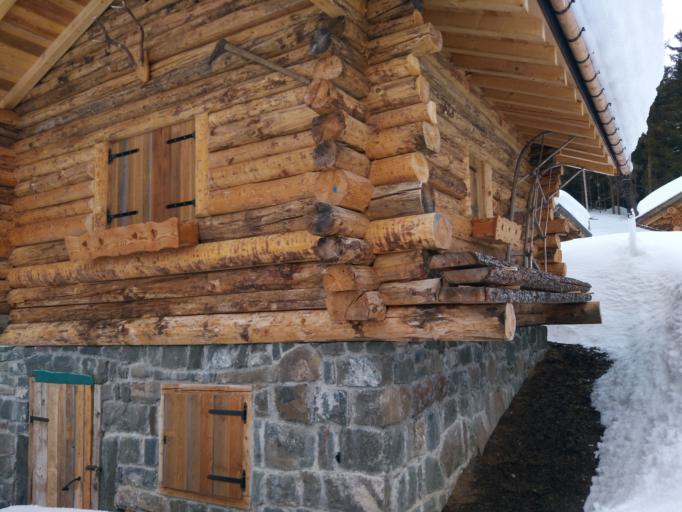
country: IT
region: Veneto
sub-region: Provincia di Belluno
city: Rocca Pietore
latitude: 46.4187
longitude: 11.9815
